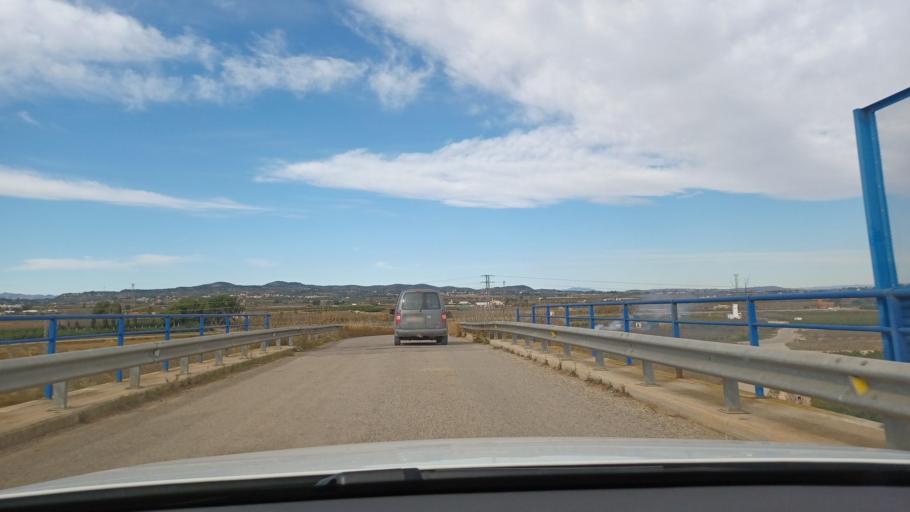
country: ES
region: Valencia
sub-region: Provincia de Valencia
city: Benifaio
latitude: 39.2918
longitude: -0.4372
